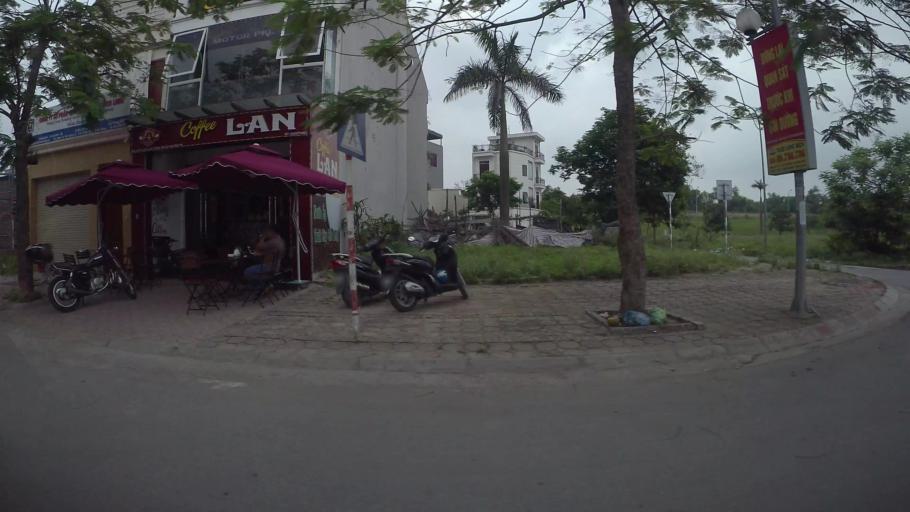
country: VN
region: Ha Noi
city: Trau Quy
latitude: 21.0565
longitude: 105.9176
